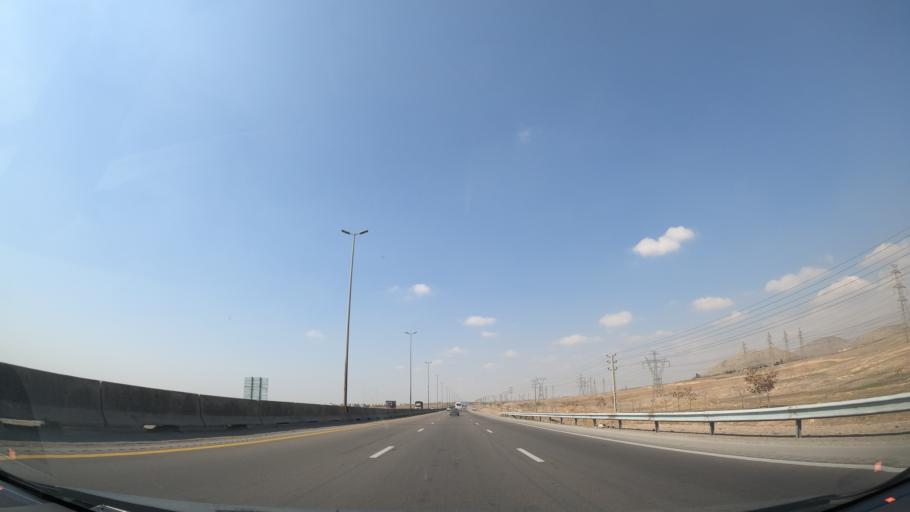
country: IR
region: Qazvin
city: Abyek
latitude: 36.0598
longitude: 50.4991
